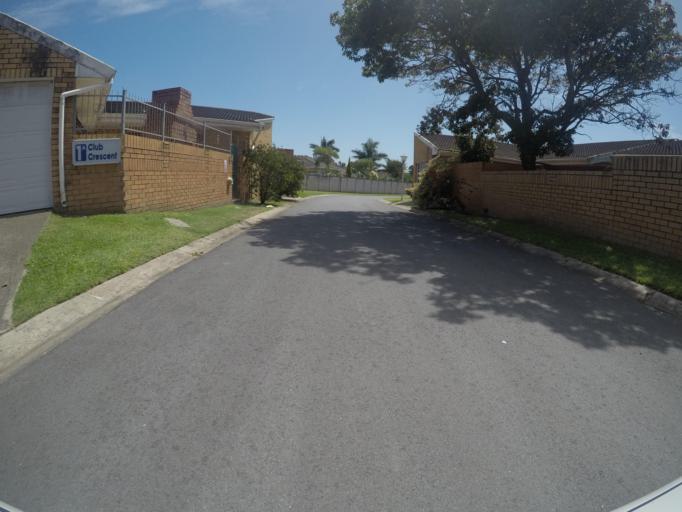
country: ZA
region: Eastern Cape
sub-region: Buffalo City Metropolitan Municipality
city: East London
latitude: -32.9521
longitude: 27.9983
